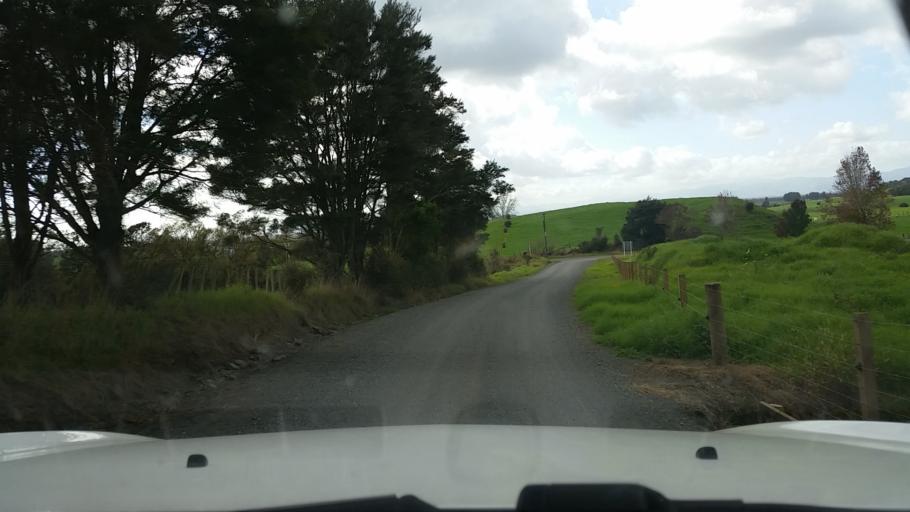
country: NZ
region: Waikato
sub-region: Hauraki District
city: Ngatea
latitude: -37.4452
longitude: 175.4861
